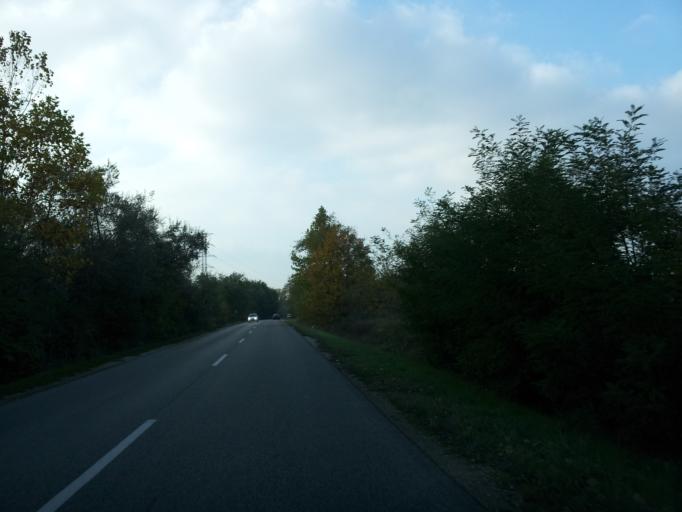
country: HU
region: Komarom-Esztergom
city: Bokod
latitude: 47.4801
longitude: 18.2789
